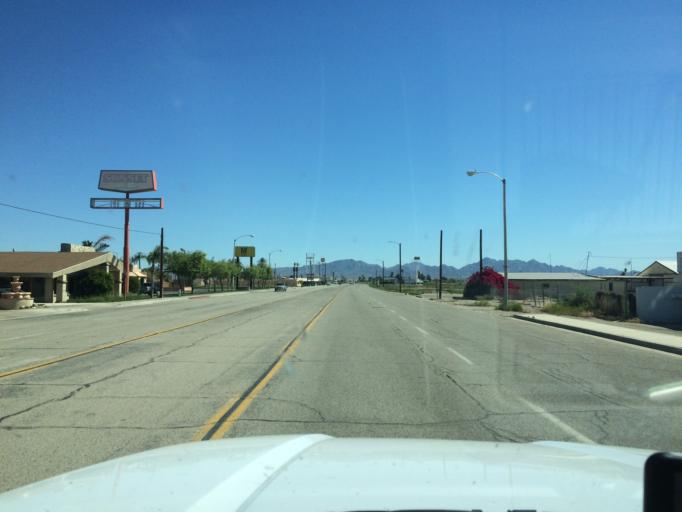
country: US
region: California
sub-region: Riverside County
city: Blythe
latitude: 33.6107
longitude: -114.5758
